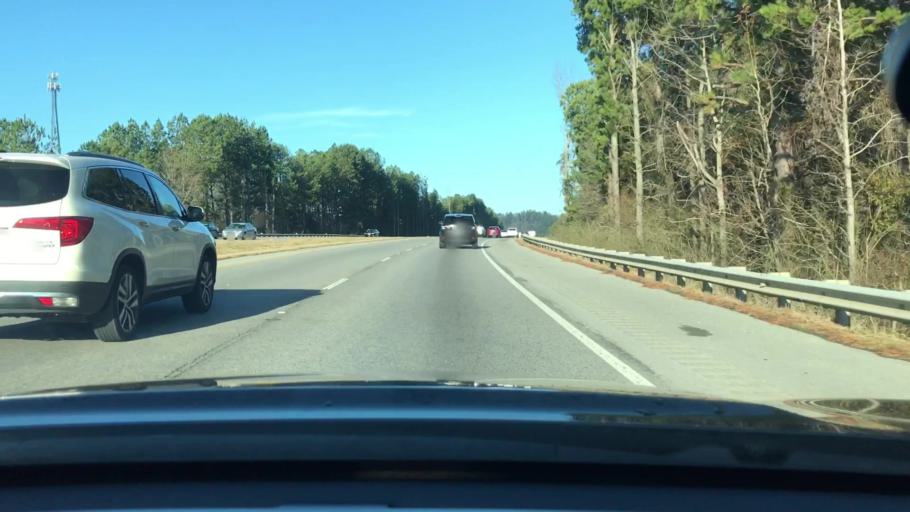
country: US
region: Alabama
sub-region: Shelby County
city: Chelsea
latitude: 33.3489
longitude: -86.6408
